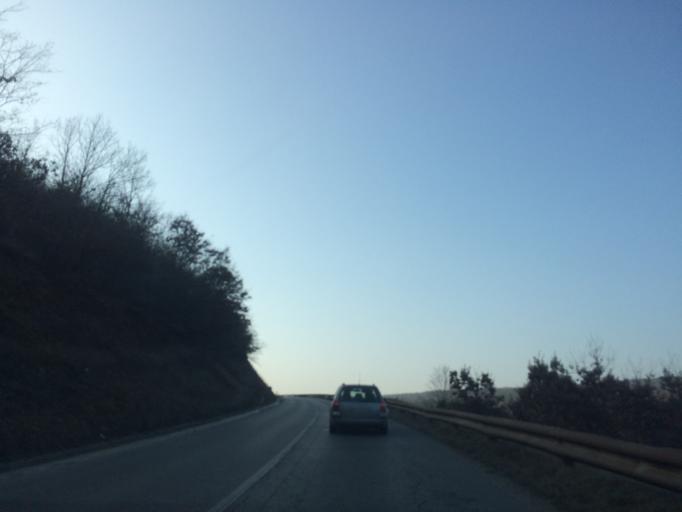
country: XK
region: Pec
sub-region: Komuna e Pejes
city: Kosuriq
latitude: 42.5042
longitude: 20.5230
